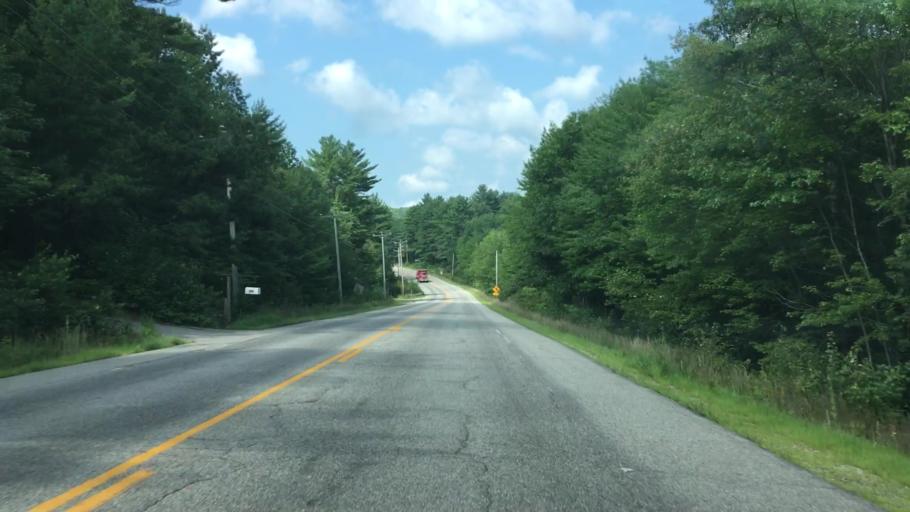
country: US
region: Maine
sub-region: Androscoggin County
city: Minot
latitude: 44.0298
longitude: -70.3407
